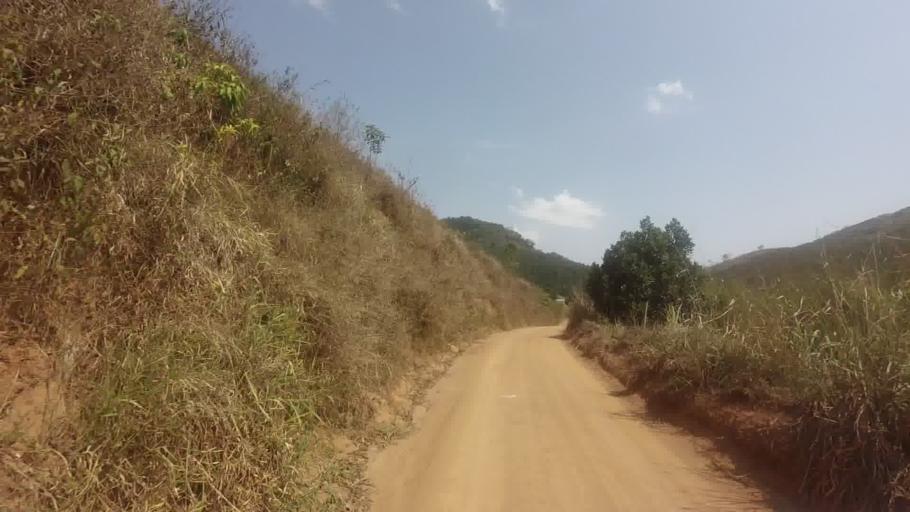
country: BR
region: Espirito Santo
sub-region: Mimoso Do Sul
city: Mimoso do Sul
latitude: -20.9956
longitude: -41.5020
